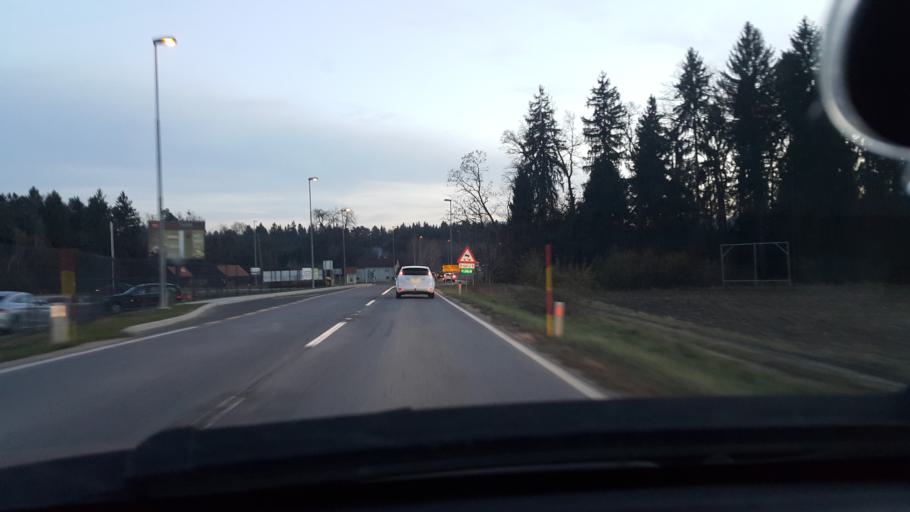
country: SI
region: Zalec
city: Zalec
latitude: 46.2714
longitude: 15.1903
